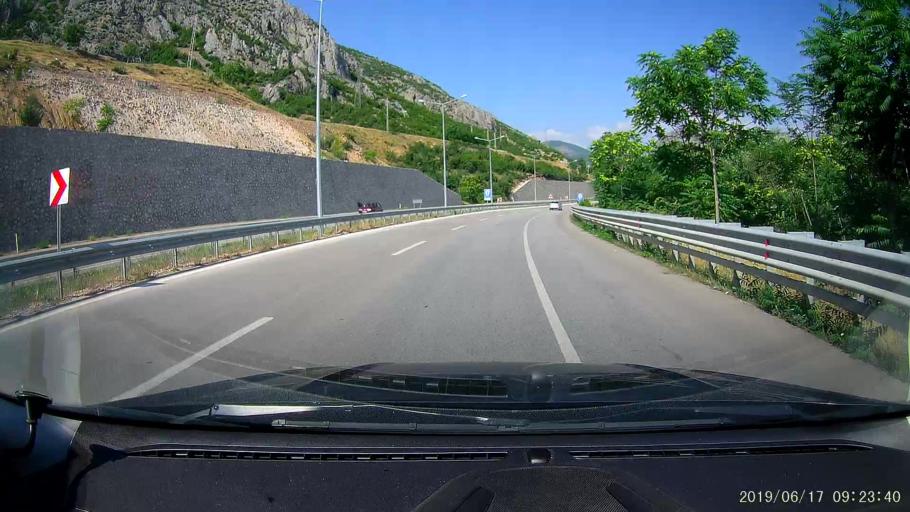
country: TR
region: Amasya
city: Amasya
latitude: 40.6742
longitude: 35.8702
